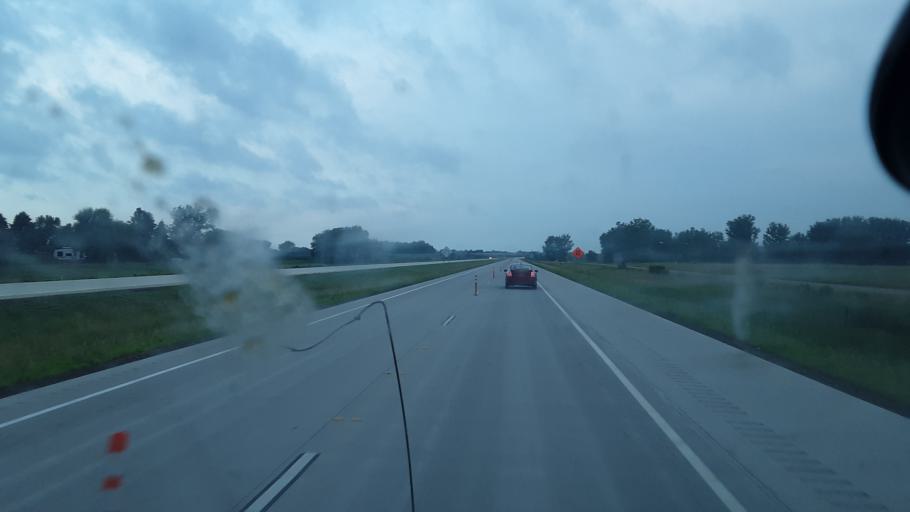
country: US
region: Minnesota
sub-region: Martin County
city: Fairmont
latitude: 43.6710
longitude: -94.3953
